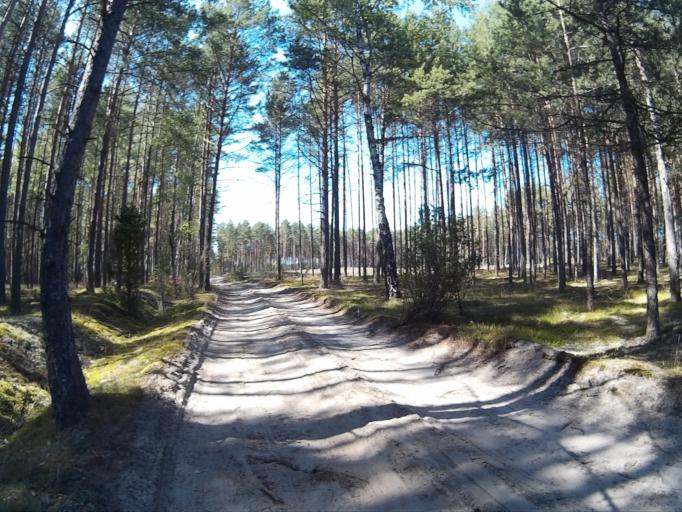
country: PL
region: Pomeranian Voivodeship
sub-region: Powiat chojnicki
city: Czersk
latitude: 53.7237
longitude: 17.9005
